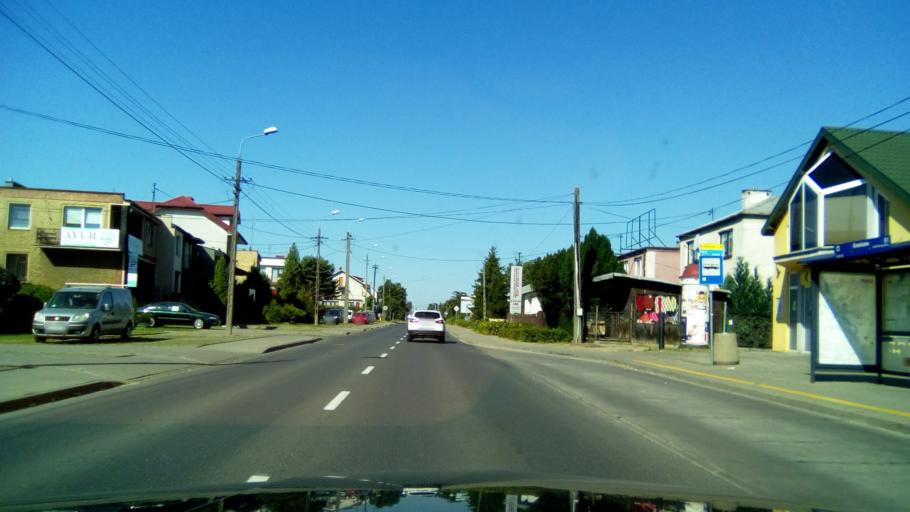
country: PL
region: Masovian Voivodeship
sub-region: Plock
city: Plock
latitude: 52.5391
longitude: 19.7291
